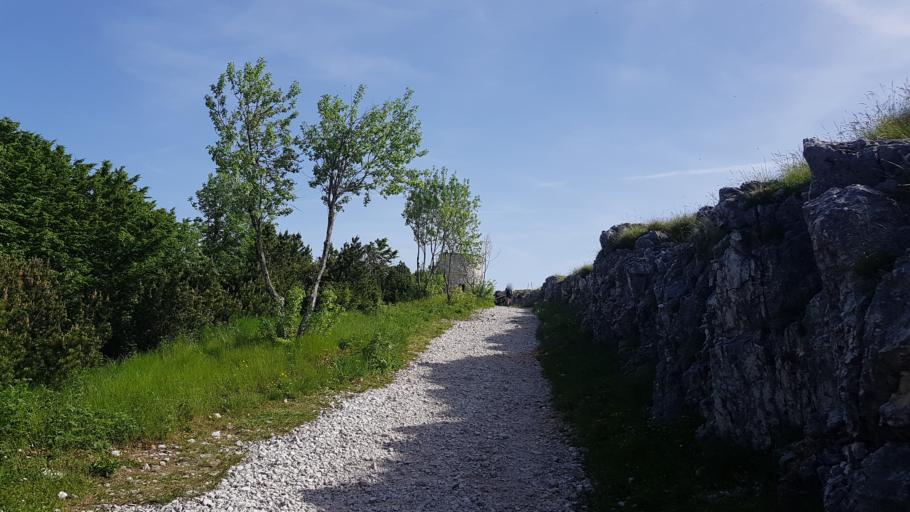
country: HR
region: Istarska
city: Lovran
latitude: 45.2857
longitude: 14.2021
